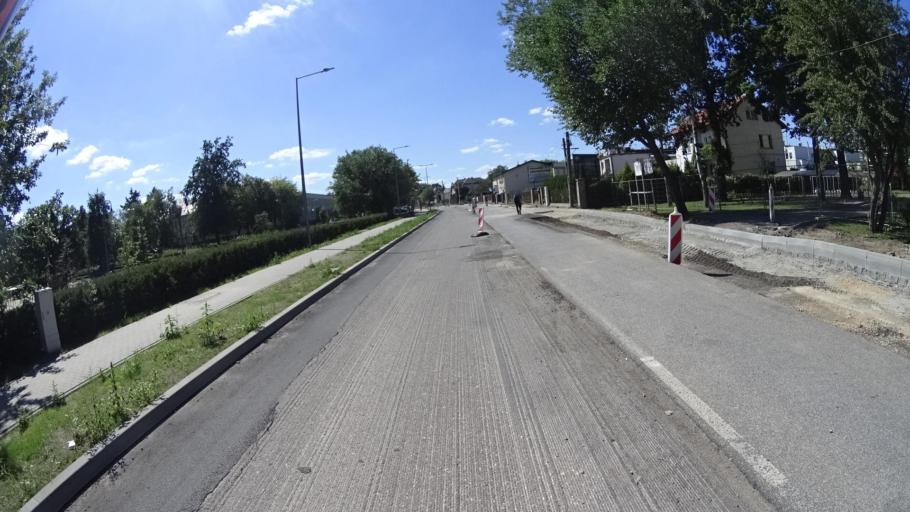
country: PL
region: Masovian Voivodeship
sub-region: Powiat piaseczynski
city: Piaseczno
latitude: 52.0764
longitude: 21.0327
